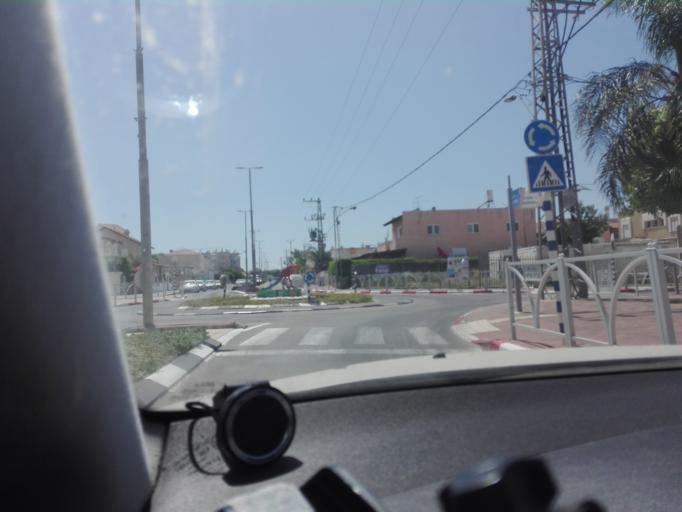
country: IL
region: Central District
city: Bene 'Ayish
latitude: 31.7346
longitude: 34.7436
